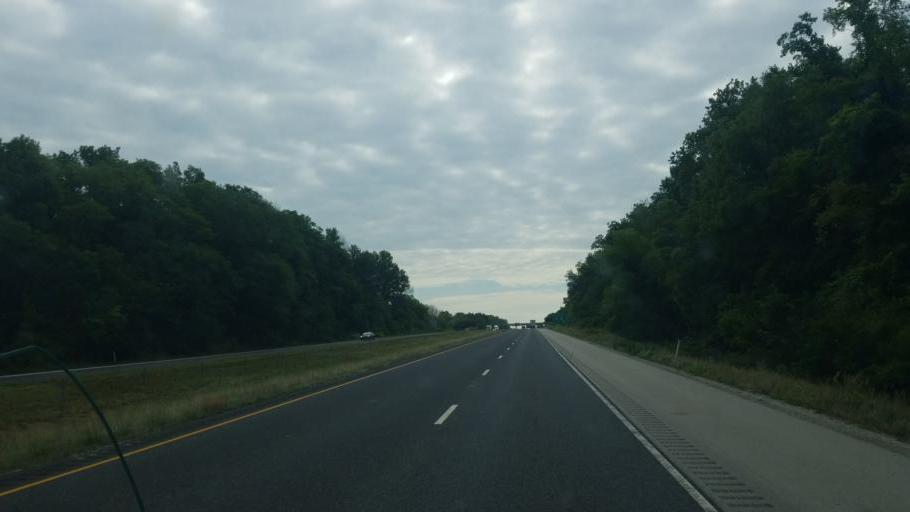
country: US
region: Indiana
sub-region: Vigo County
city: Terre Haute
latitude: 39.4307
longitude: -87.3680
